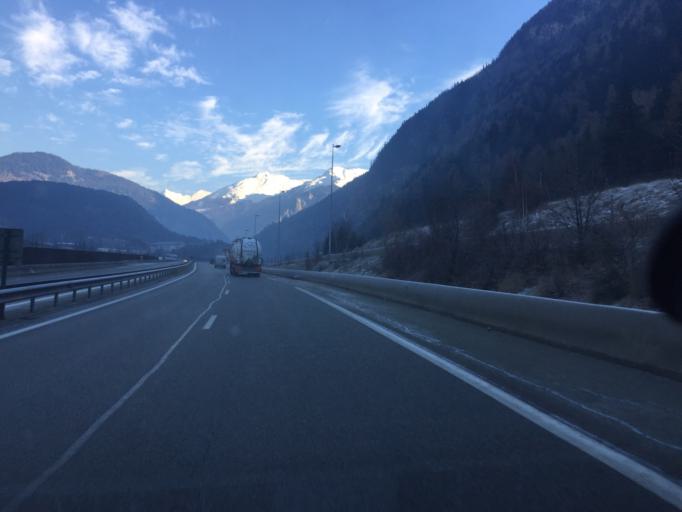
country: FR
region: Rhone-Alpes
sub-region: Departement de la Savoie
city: Modane
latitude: 45.2019
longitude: 6.5896
